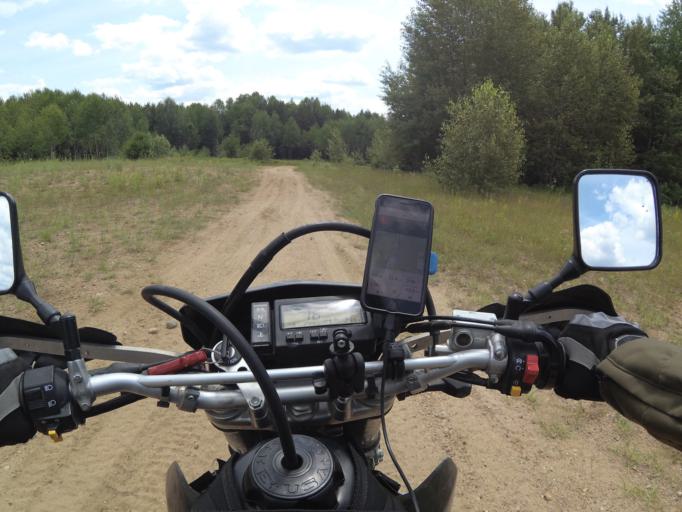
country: CA
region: Ontario
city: Bancroft
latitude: 45.0268
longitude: -77.2649
